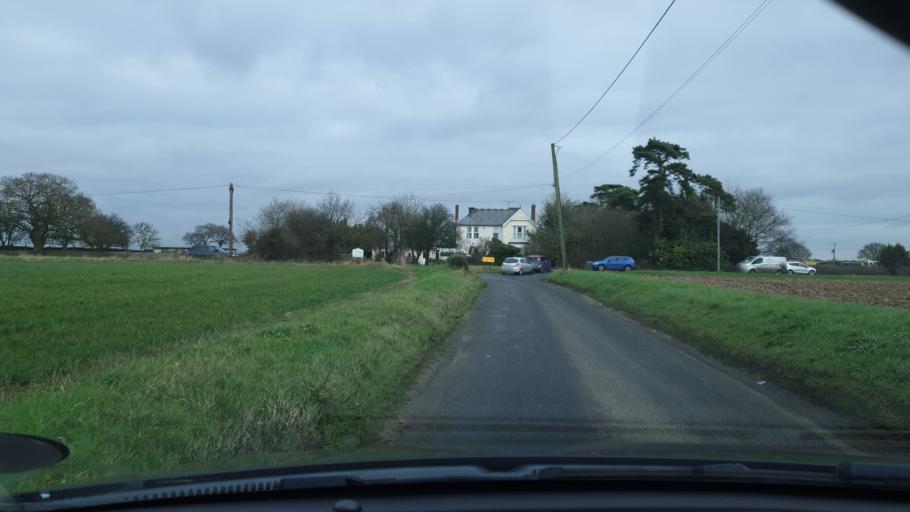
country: GB
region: England
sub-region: Essex
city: Frinton-on-Sea
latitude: 51.8462
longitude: 1.1946
